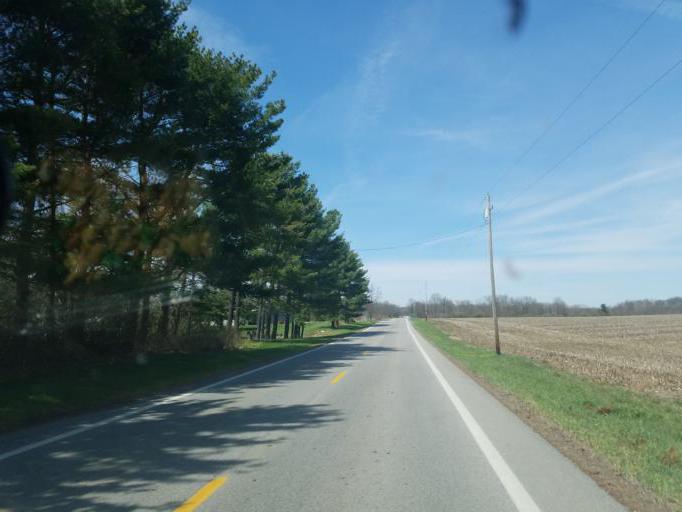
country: US
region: Ohio
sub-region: Delaware County
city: Ashley
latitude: 40.4258
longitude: -83.0369
